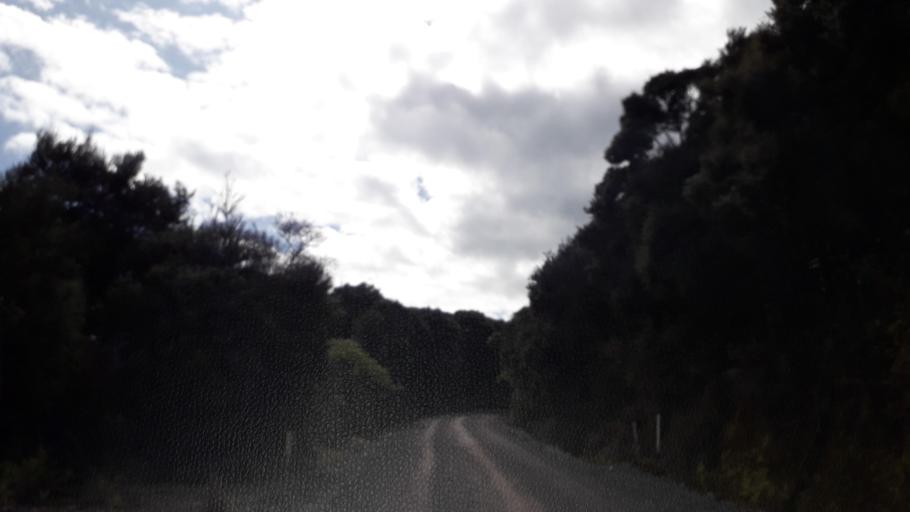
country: NZ
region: Northland
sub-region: Far North District
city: Paihia
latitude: -35.2976
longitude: 174.2182
